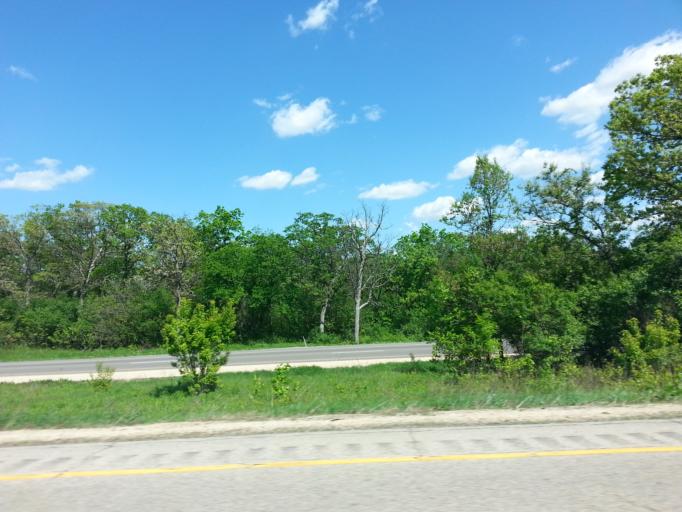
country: US
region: Wisconsin
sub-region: Rock County
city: Janesville
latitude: 42.7439
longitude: -89.0055
